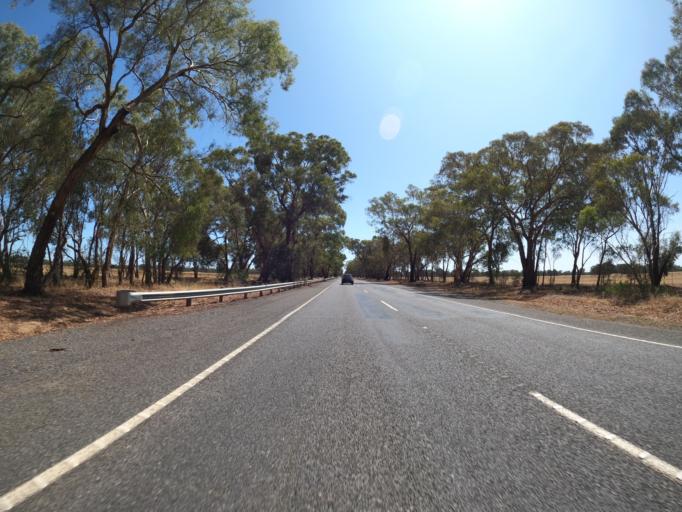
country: AU
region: New South Wales
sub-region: Corowa Shire
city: Corowa
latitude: -36.0601
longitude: 146.4178
